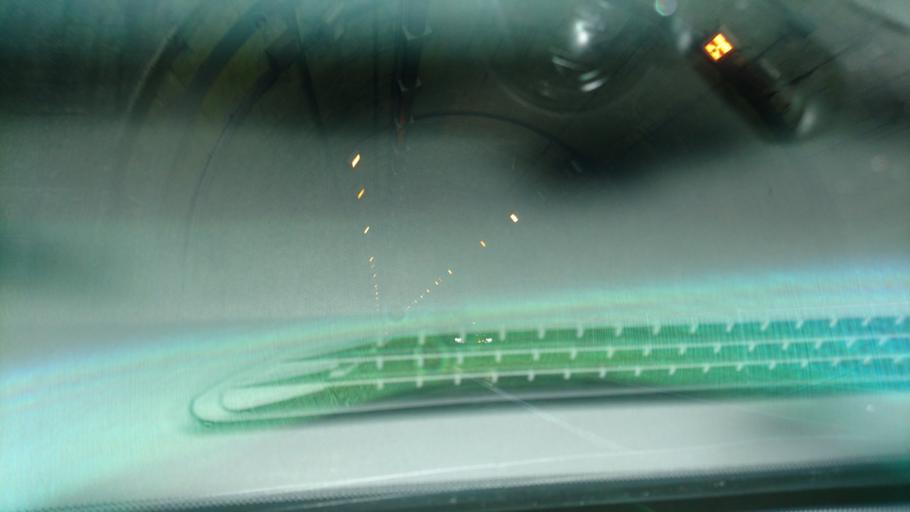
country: JP
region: Iwate
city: Kamaishi
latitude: 39.1987
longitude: 141.8613
